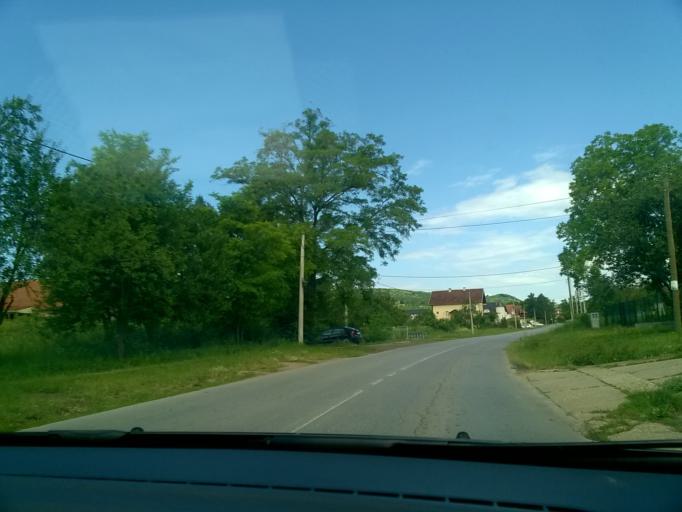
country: RS
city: Vrdnik
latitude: 45.1153
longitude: 19.7957
